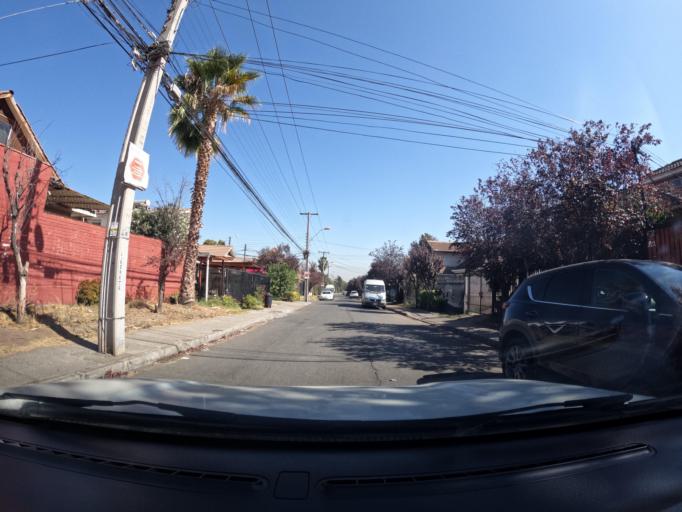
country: CL
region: Santiago Metropolitan
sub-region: Provincia de Santiago
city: Villa Presidente Frei, Nunoa, Santiago, Chile
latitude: -33.4774
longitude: -70.5532
